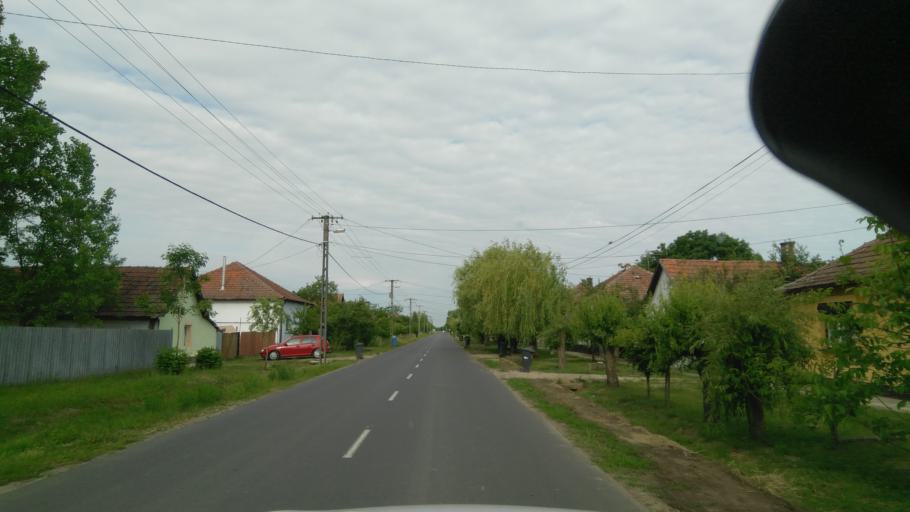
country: HU
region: Bekes
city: Ketegyhaza
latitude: 46.5397
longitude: 21.1608
